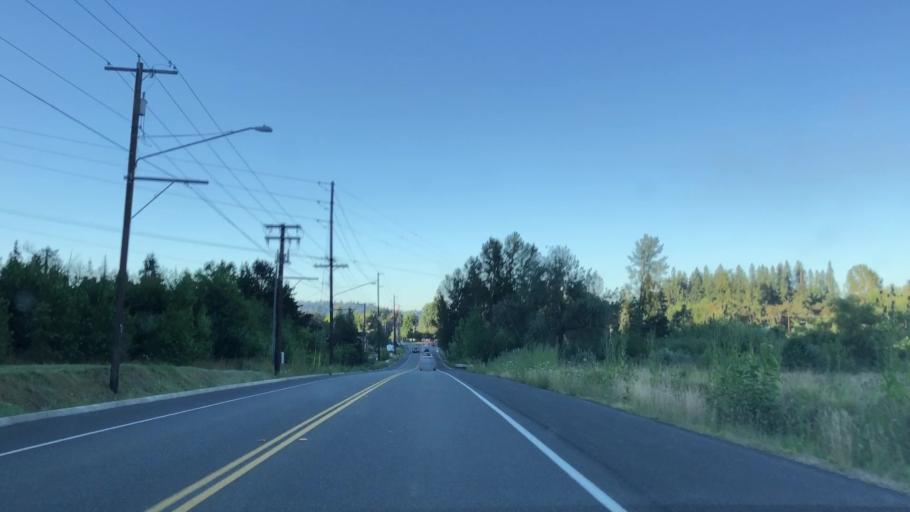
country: US
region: Washington
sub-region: King County
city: Sammamish
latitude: 47.6796
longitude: -122.0791
